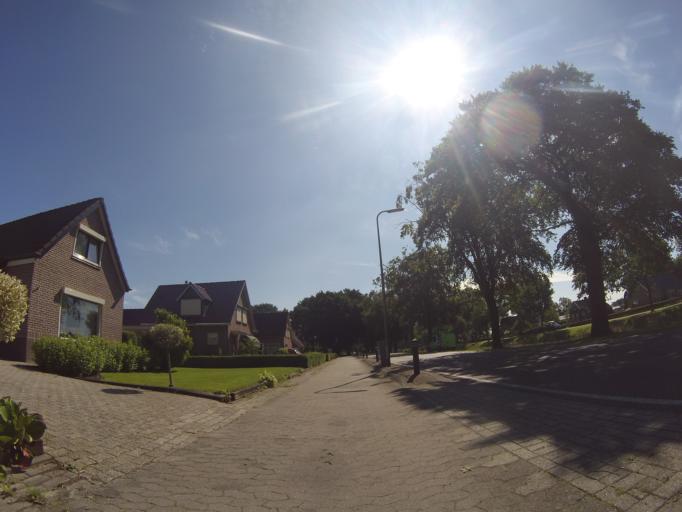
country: NL
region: Drenthe
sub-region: Gemeente Emmen
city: Schoonebeek
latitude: 52.7136
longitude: 6.8836
